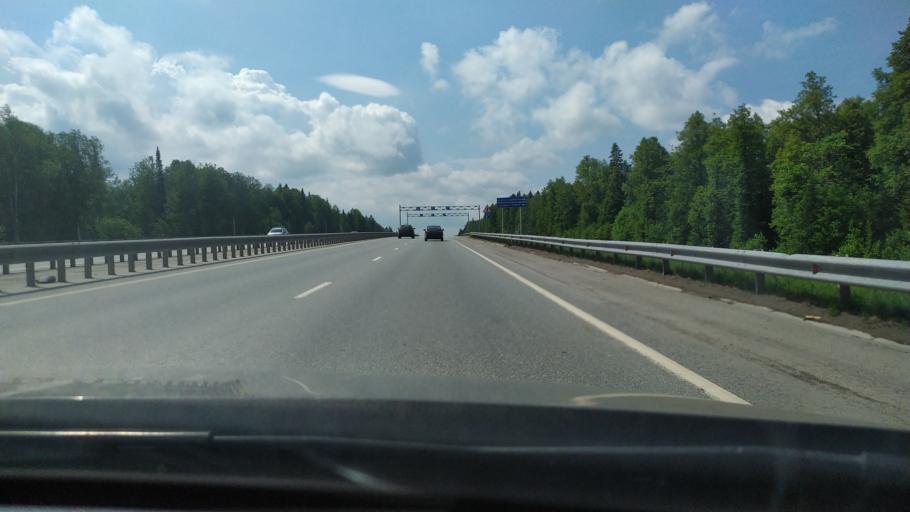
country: RU
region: Perm
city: Ferma
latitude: 58.0283
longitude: 56.4297
